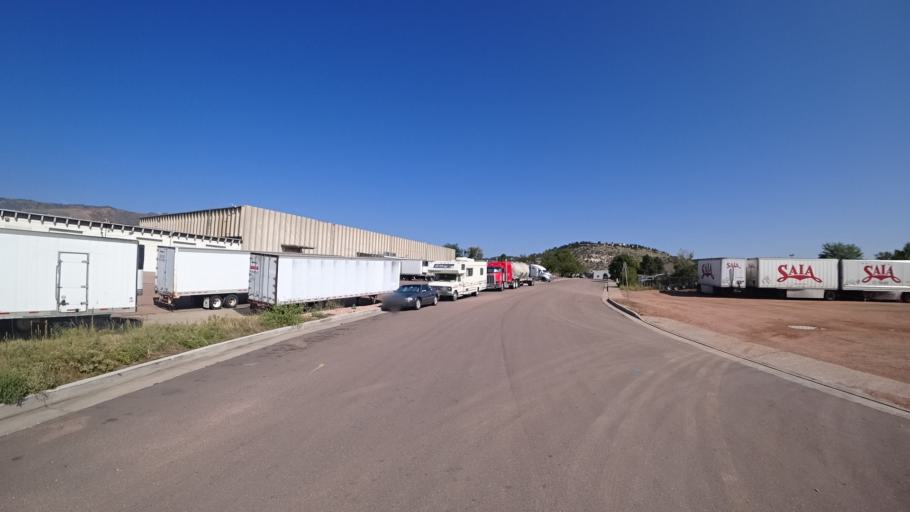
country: US
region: Colorado
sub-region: El Paso County
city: Colorado Springs
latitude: 38.8946
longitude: -104.8482
